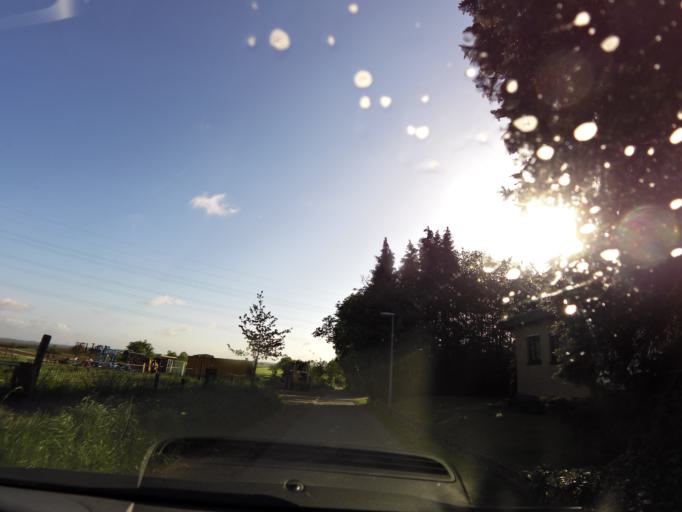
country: NL
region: Limburg
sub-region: Gemeente Voerendaal
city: Ubachsberg
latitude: 50.8560
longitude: 5.9507
